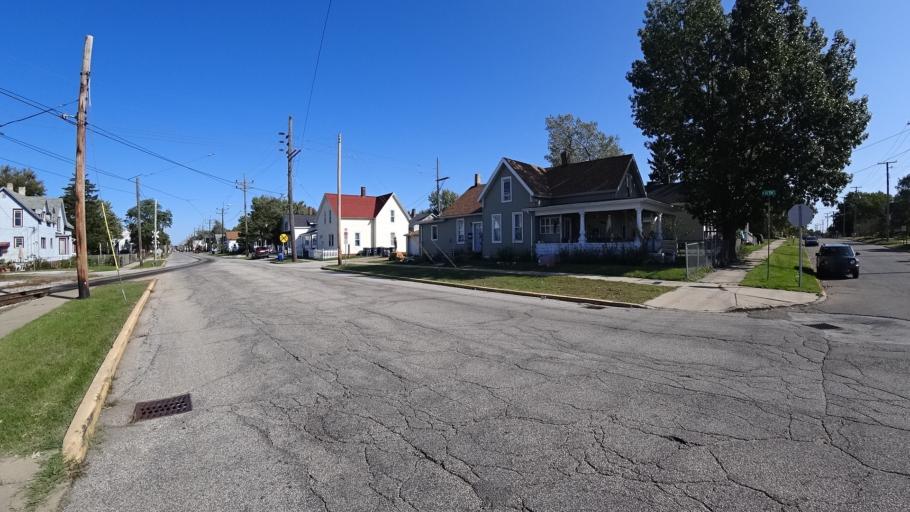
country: US
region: Indiana
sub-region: LaPorte County
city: Michigan City
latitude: 41.7090
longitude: -86.9078
